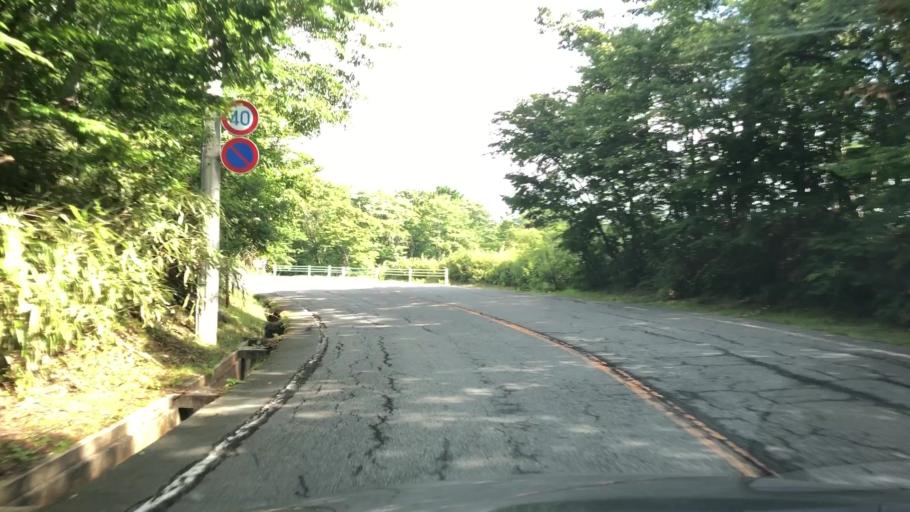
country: JP
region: Shizuoka
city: Gotemba
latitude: 35.3329
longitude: 138.8093
